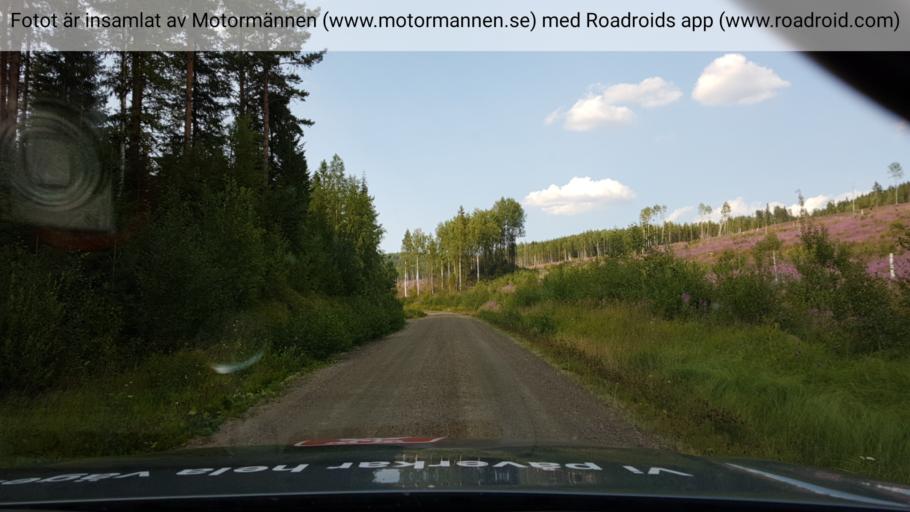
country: SE
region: Jaemtland
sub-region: Bergs Kommun
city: Hoverberg
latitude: 62.5270
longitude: 14.9152
